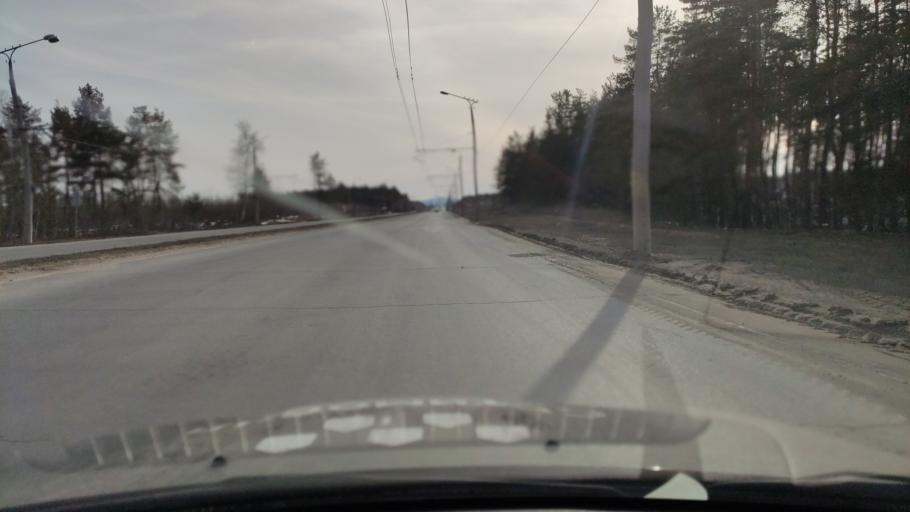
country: RU
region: Samara
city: Zhigulevsk
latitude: 53.5302
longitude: 49.5532
